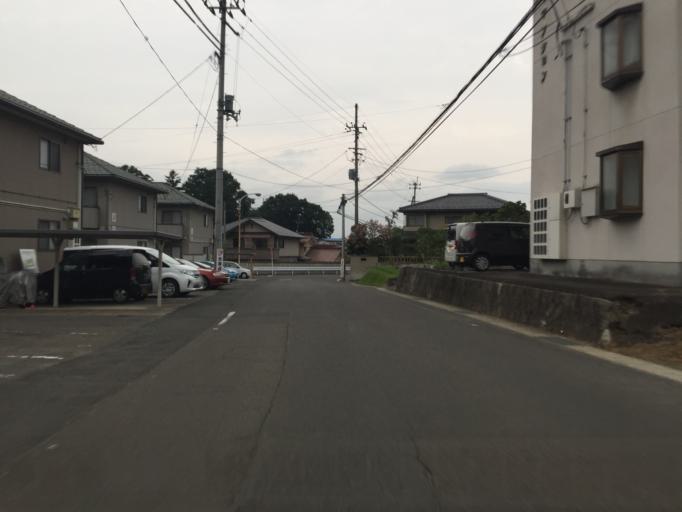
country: JP
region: Fukushima
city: Fukushima-shi
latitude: 37.7205
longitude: 140.4580
